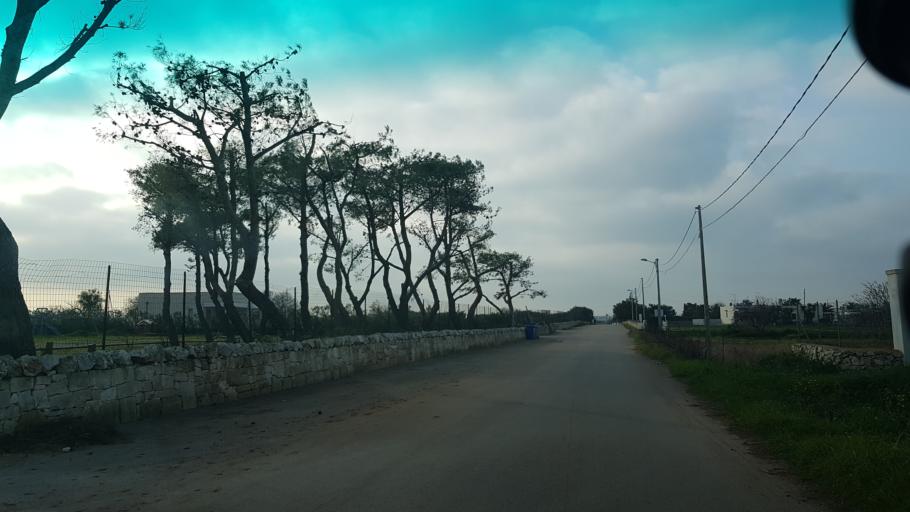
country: IT
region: Apulia
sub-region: Provincia di Brindisi
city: Carovigno
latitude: 40.7435
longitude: 17.7270
